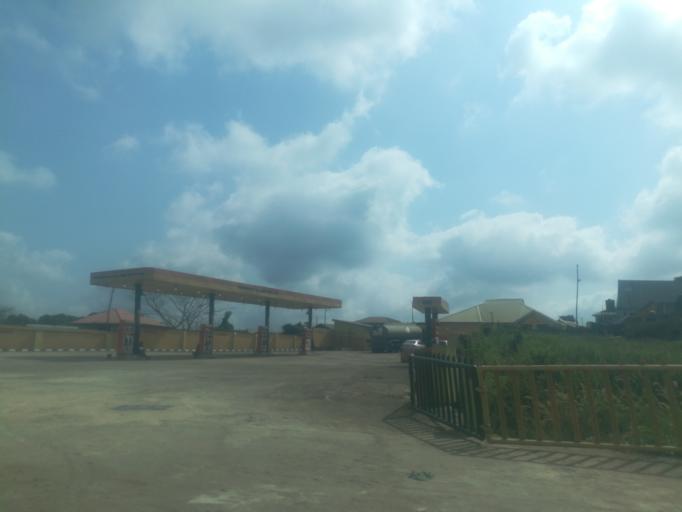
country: NG
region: Oyo
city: Moniya
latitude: 7.5350
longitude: 3.9165
